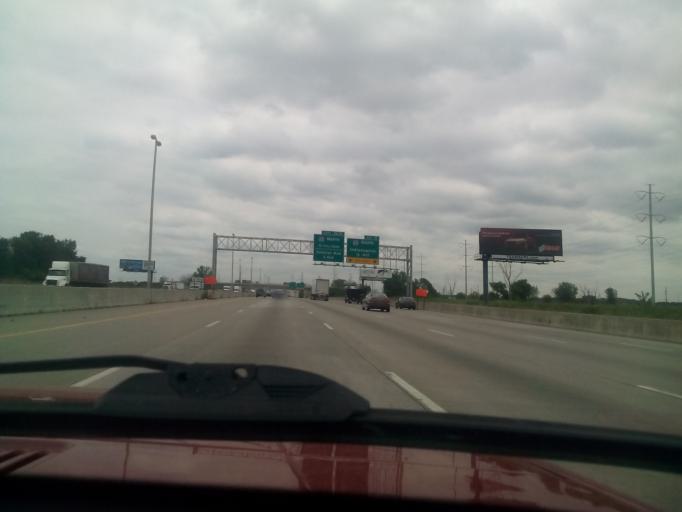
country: US
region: Indiana
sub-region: Lake County
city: Gary
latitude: 41.5673
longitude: -87.3244
